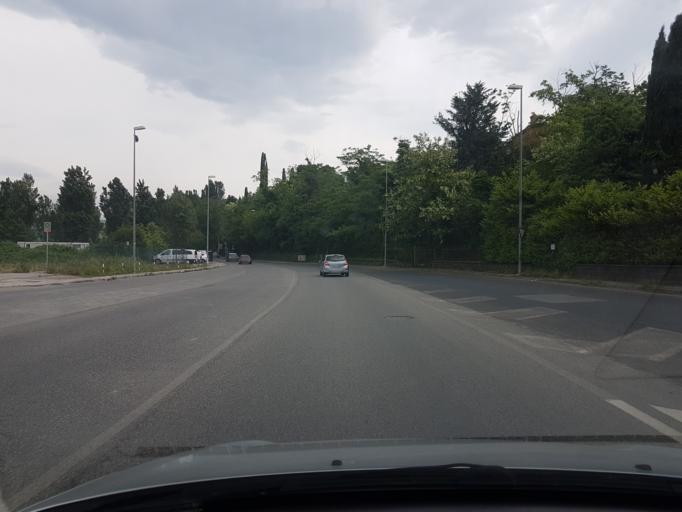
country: IT
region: Friuli Venezia Giulia
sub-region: Provincia di Trieste
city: Muggia
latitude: 45.5984
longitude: 13.7815
